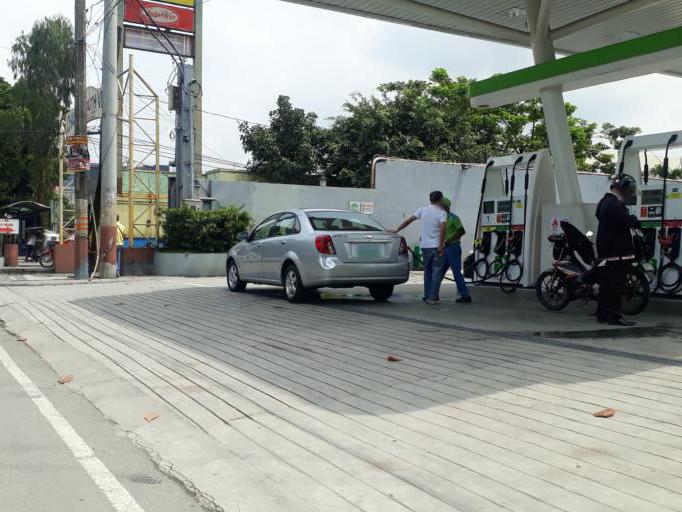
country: PH
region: Metro Manila
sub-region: Marikina
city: Calumpang
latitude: 14.6163
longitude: 121.0925
